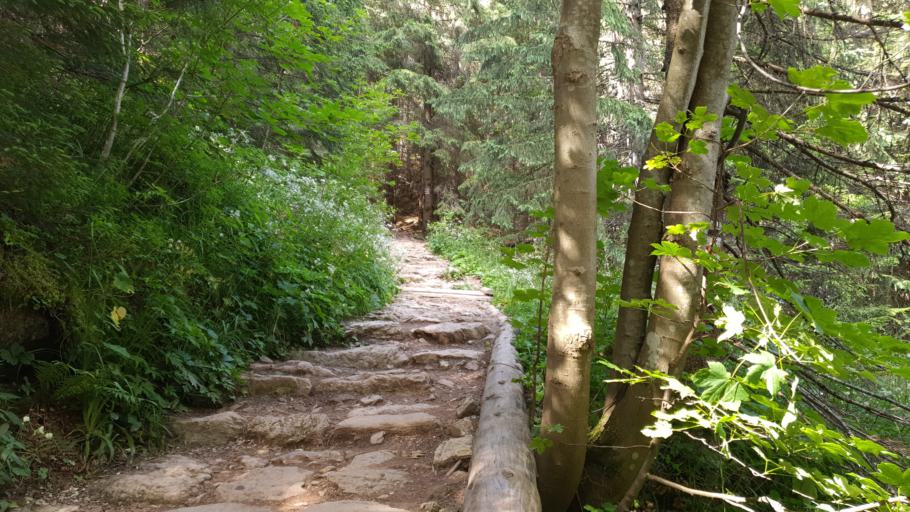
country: PL
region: Lesser Poland Voivodeship
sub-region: Powiat tatrzanski
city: Koscielisko
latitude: 49.2602
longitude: 19.9209
